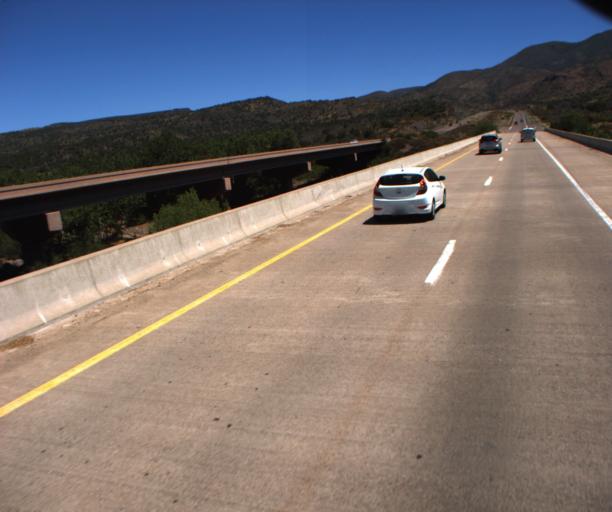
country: US
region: Arizona
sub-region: Gila County
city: Tonto Basin
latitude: 33.8677
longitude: -111.4673
